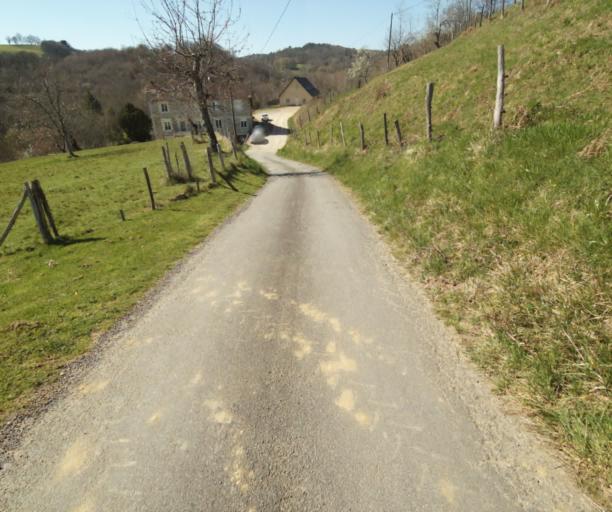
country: FR
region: Limousin
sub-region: Departement de la Correze
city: Chameyrat
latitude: 45.2552
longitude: 1.7269
